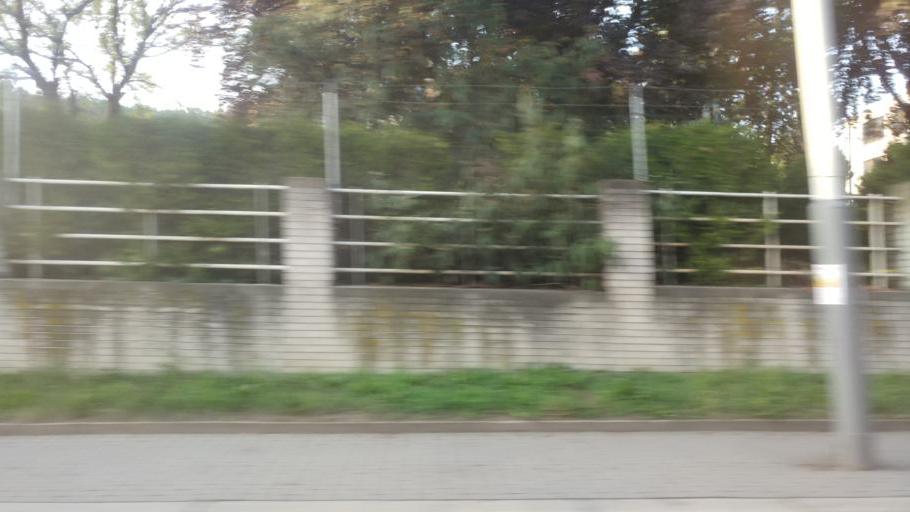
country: CZ
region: Praha
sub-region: Praha 8
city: Karlin
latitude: 50.1173
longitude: 14.4307
